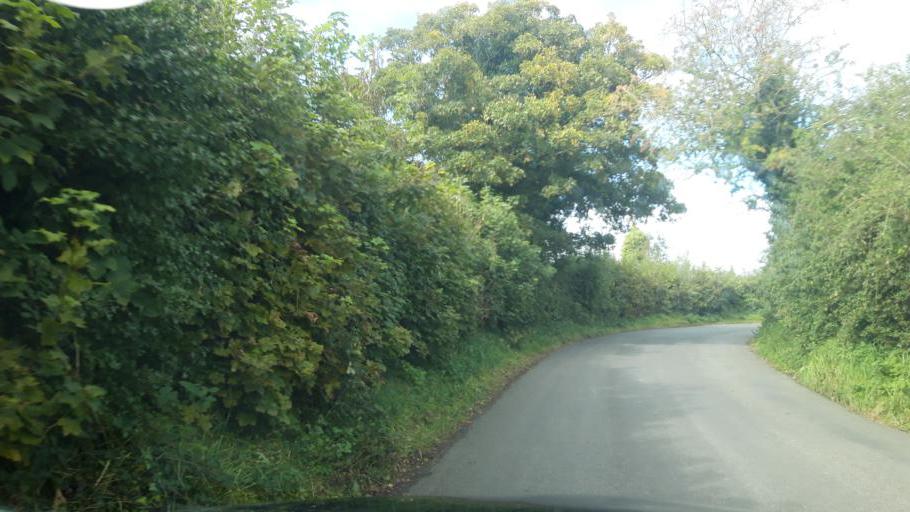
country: IE
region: Leinster
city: Ballymun
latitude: 53.4603
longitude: -6.2956
